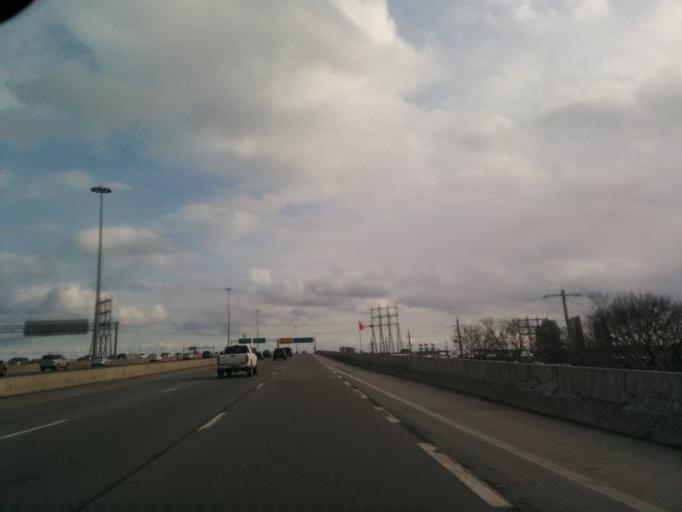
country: CA
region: Ontario
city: Etobicoke
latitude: 43.6247
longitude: -79.5558
